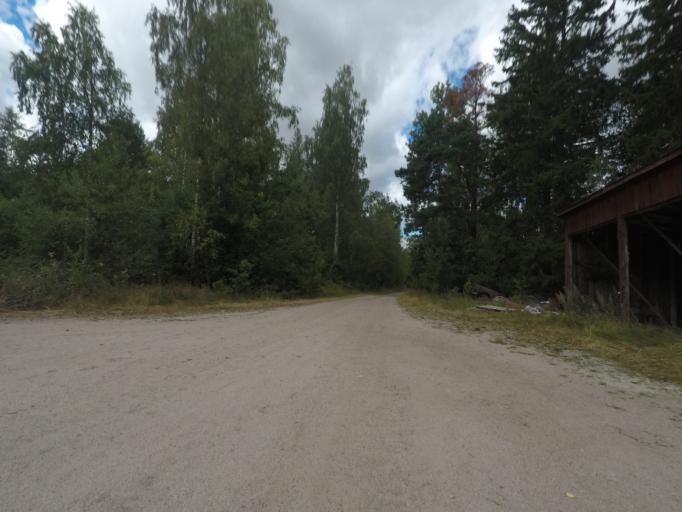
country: SE
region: Soedermanland
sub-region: Eskilstuna Kommun
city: Kvicksund
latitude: 59.4015
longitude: 16.2541
